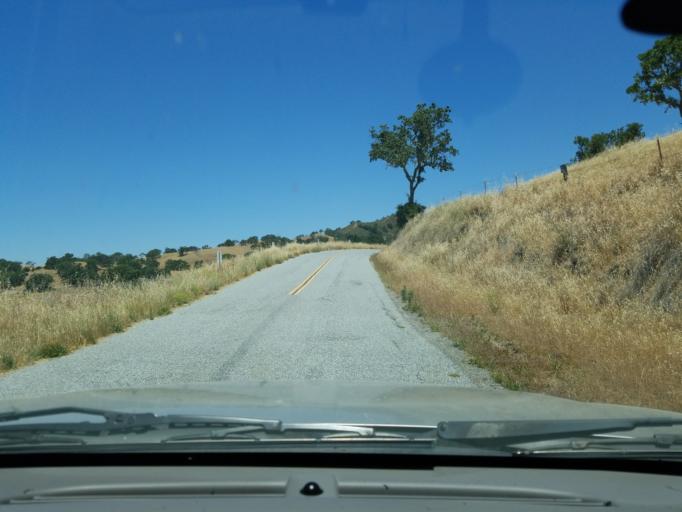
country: US
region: California
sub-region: Monterey County
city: Gonzales
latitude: 36.3978
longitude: -121.5766
